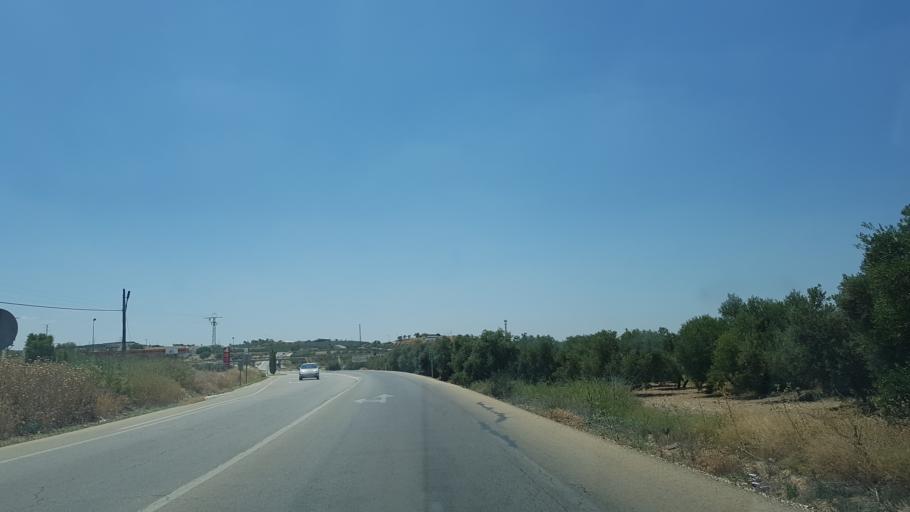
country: ES
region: Andalusia
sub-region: Provincia de Sevilla
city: Herrera
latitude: 37.3666
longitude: -4.8166
